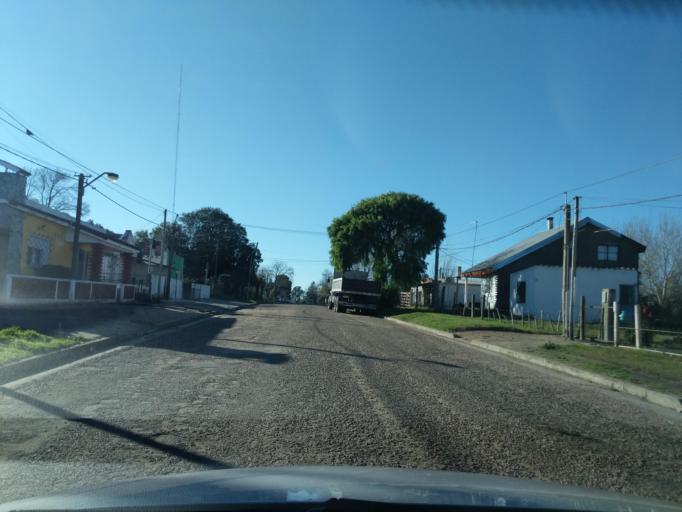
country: UY
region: Florida
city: Florida
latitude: -34.0950
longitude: -56.2395
